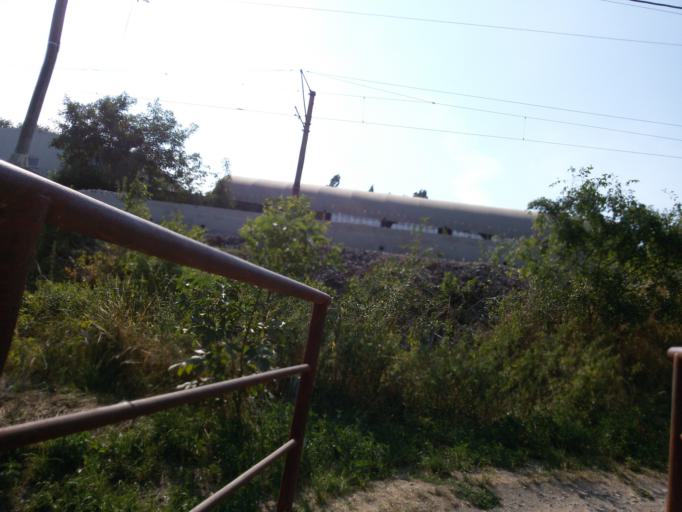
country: CZ
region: South Moravian
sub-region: Mesto Brno
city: Mokra Hora
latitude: 49.2480
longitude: 16.5901
